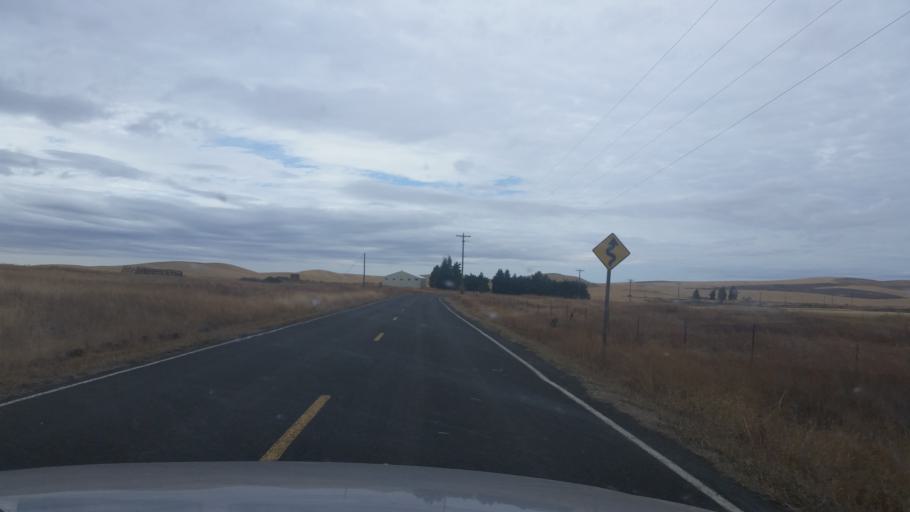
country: US
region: Washington
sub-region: Spokane County
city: Medical Lake
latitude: 47.5176
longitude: -117.8931
